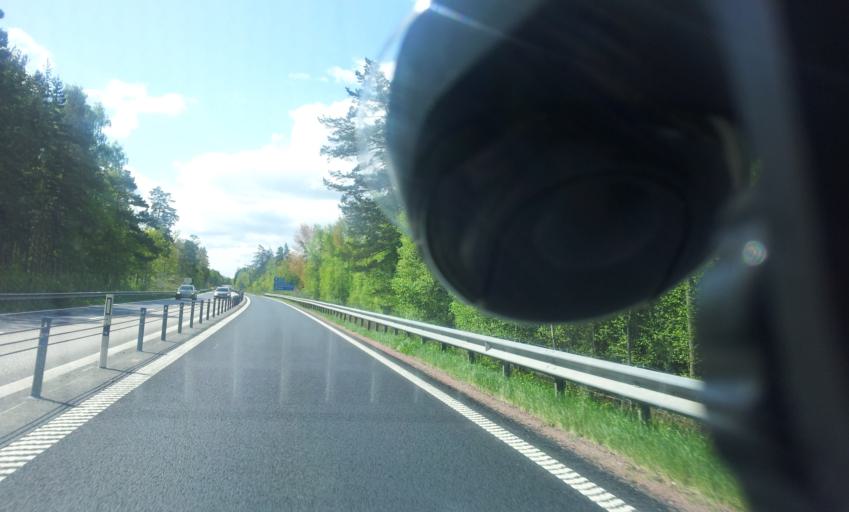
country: SE
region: Kalmar
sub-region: Monsteras Kommun
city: Timmernabben
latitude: 56.9007
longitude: 16.3789
